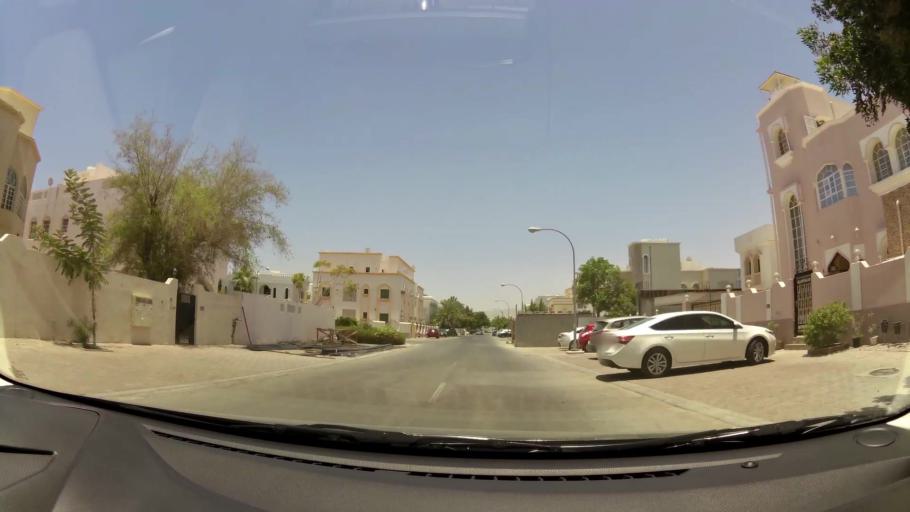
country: OM
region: Muhafazat Masqat
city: Bawshar
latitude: 23.5960
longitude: 58.3924
